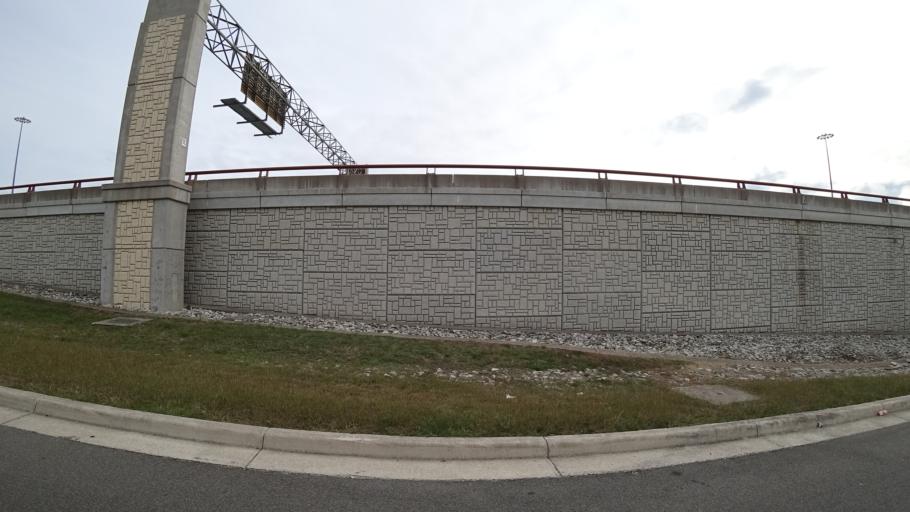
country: US
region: Texas
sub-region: Williamson County
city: Round Rock
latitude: 30.4785
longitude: -97.6924
